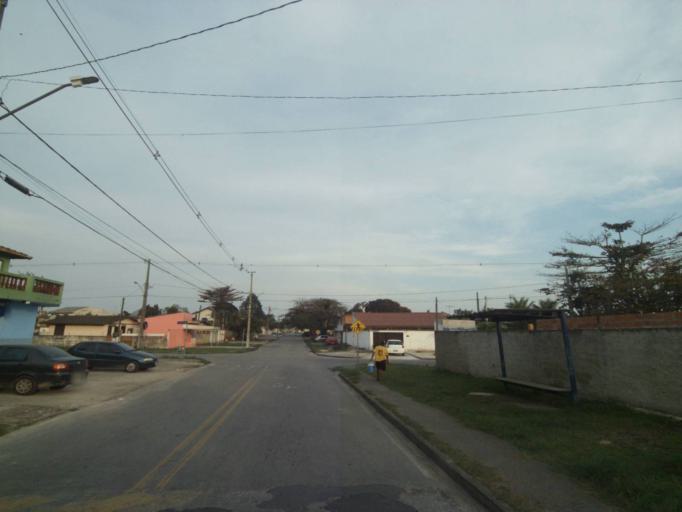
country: BR
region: Parana
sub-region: Paranagua
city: Paranagua
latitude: -25.5226
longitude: -48.5357
